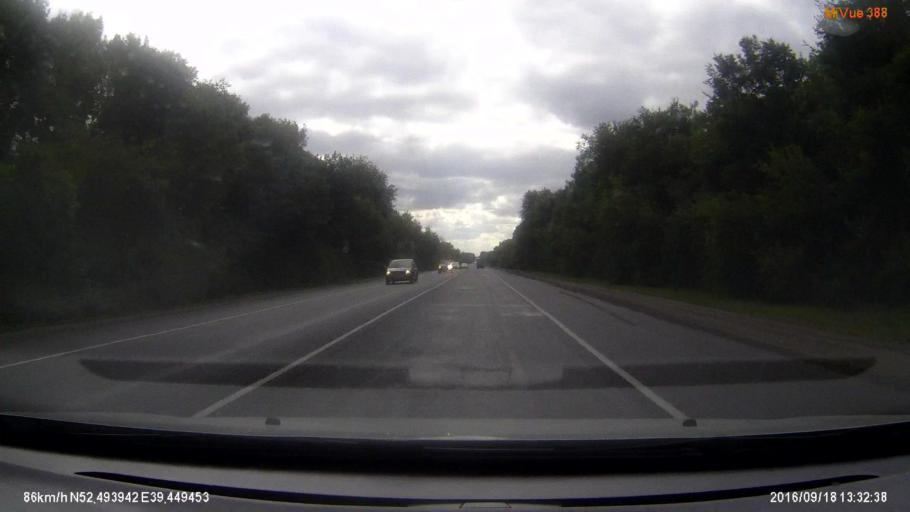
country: RU
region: Lipetsk
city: Borinskoye
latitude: 52.4712
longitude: 39.4210
